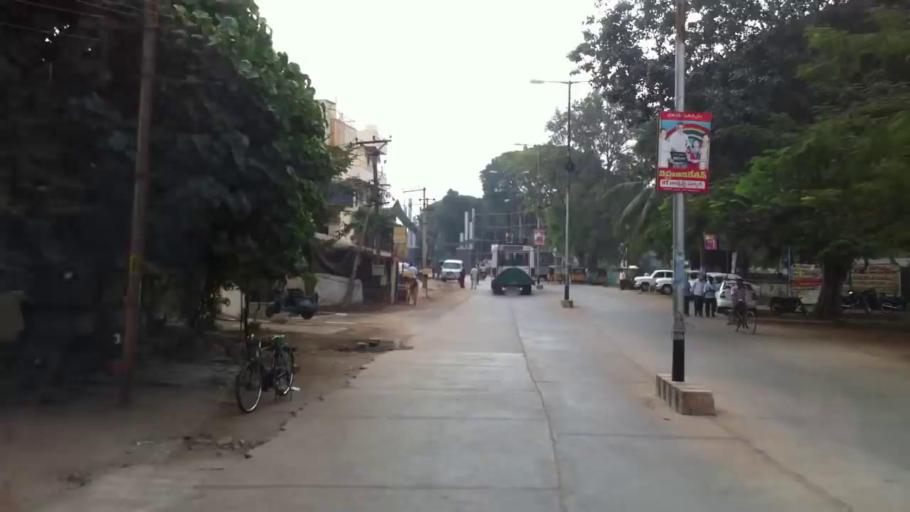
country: IN
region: Andhra Pradesh
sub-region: Guntur
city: Bhattiprolu
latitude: 16.2288
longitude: 80.6515
